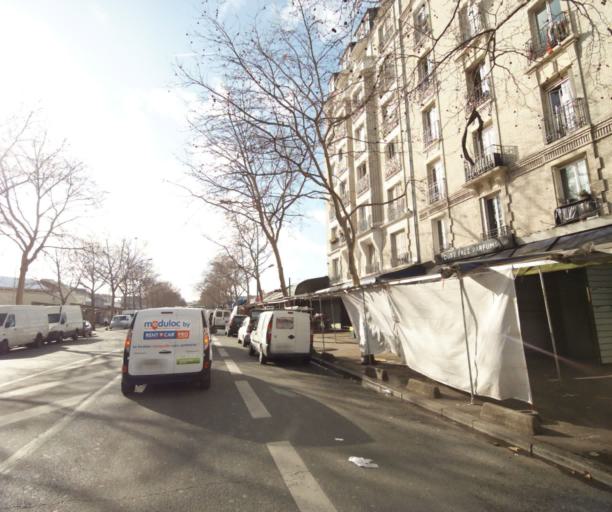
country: FR
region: Ile-de-France
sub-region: Paris
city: Saint-Ouen
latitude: 48.9037
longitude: 2.3441
